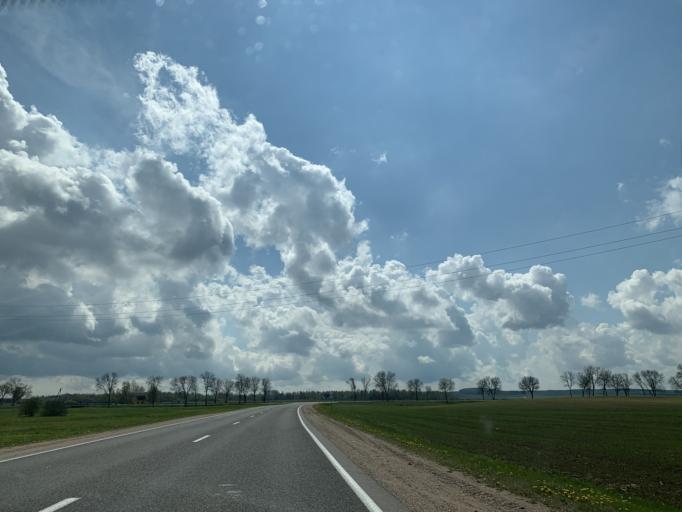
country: BY
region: Minsk
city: Nyasvizh
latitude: 53.2315
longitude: 26.7221
